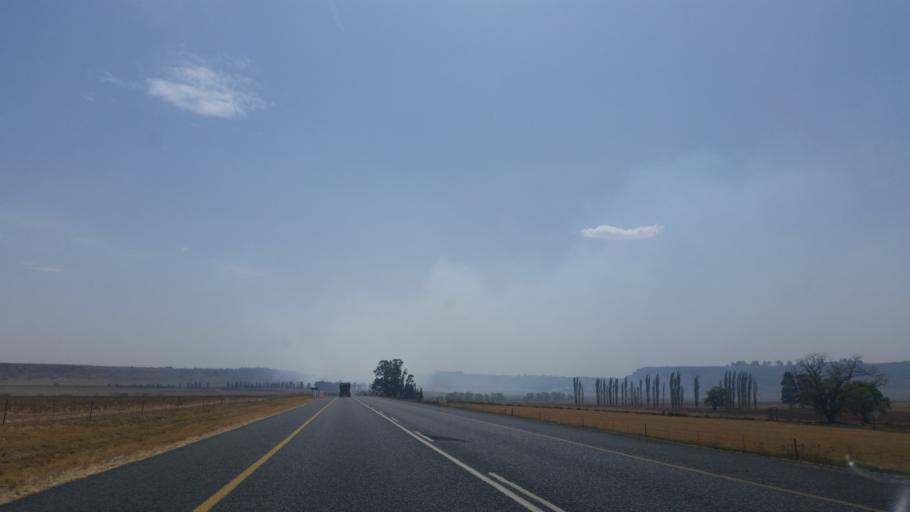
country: ZA
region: Orange Free State
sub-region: Thabo Mofutsanyana District Municipality
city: Bethlehem
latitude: -28.2778
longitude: 28.3835
